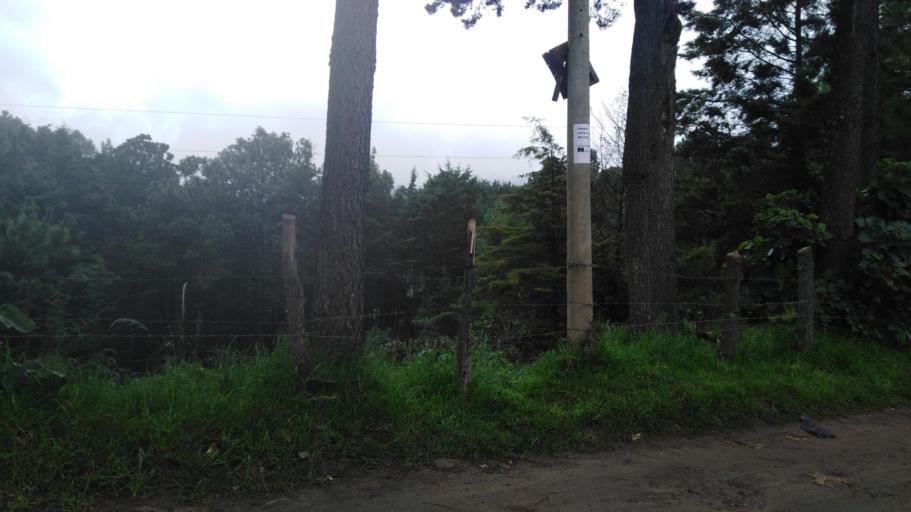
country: GT
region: Quetzaltenango
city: Olintepeque
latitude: 14.8591
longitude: -91.5037
